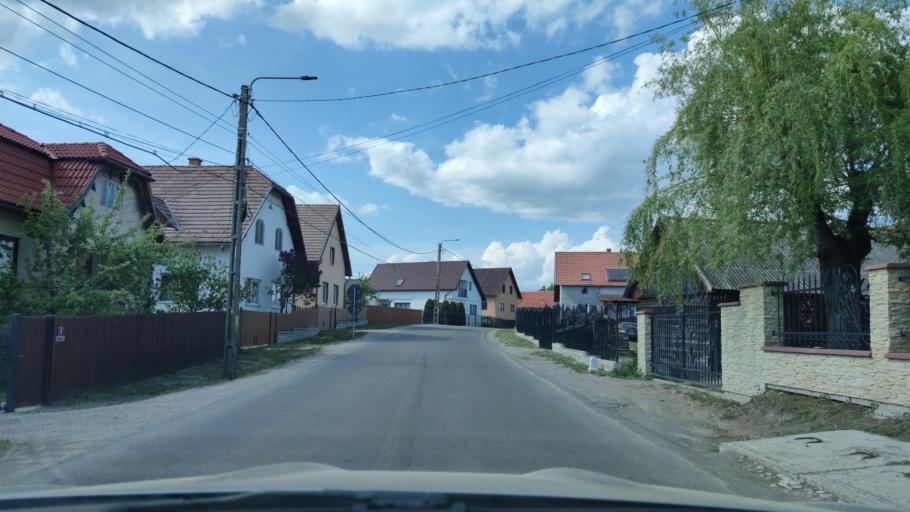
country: RO
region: Harghita
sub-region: Comuna Remetea
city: Remetea
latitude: 46.7994
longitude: 25.4572
